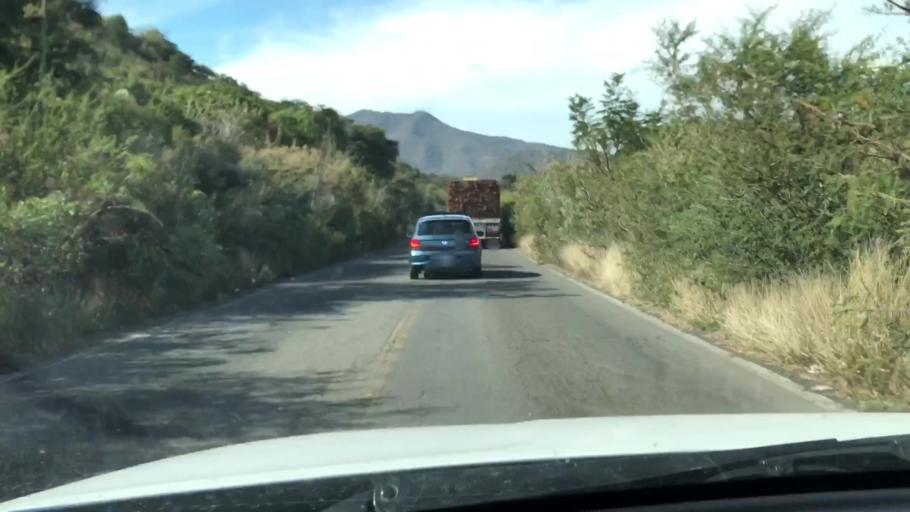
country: MX
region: Jalisco
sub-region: Zacoalco de Torres
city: Barranca de Otates (Barranca de Otatan)
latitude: 20.2285
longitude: -103.6794
